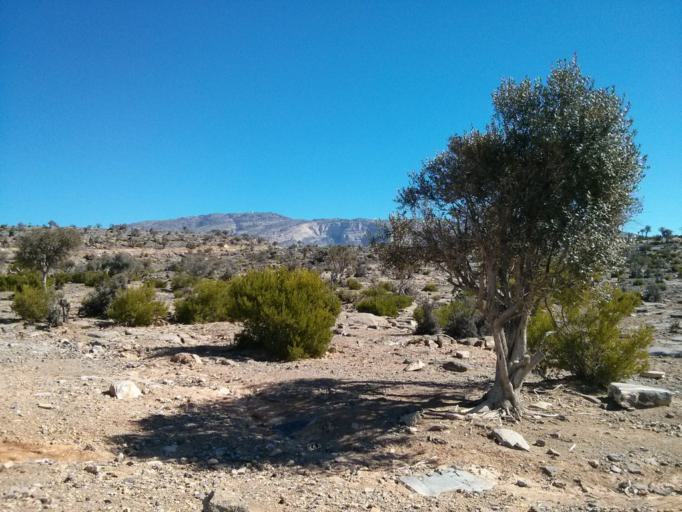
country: OM
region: Muhafazat ad Dakhiliyah
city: Bahla'
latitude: 23.2078
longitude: 57.1983
